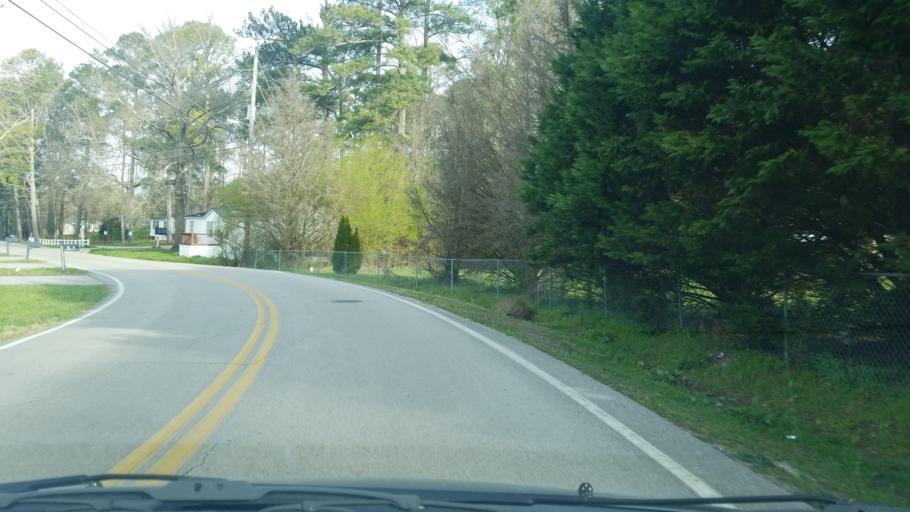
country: US
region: Tennessee
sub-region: Hamilton County
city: Collegedale
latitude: 35.0585
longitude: -85.1071
